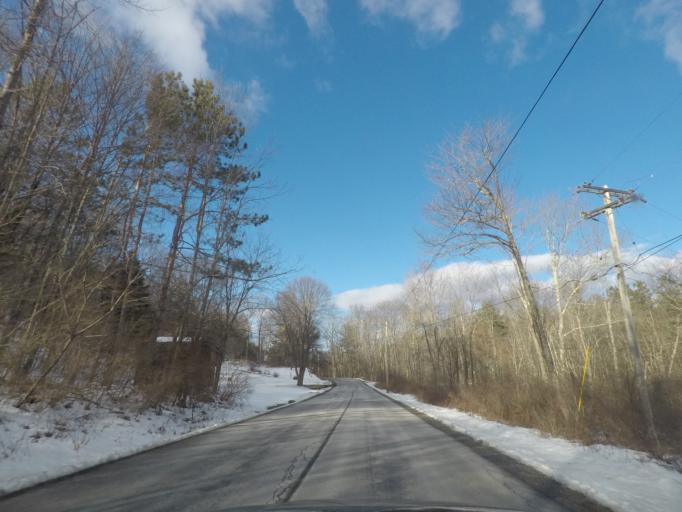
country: US
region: New York
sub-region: Rensselaer County
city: Nassau
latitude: 42.5338
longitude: -73.5286
